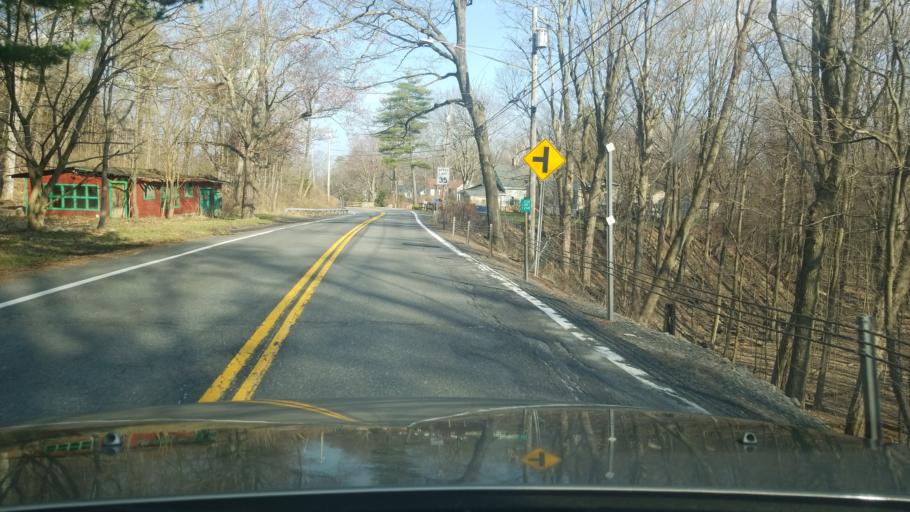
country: US
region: New York
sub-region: Greene County
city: Palenville
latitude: 42.1756
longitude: -74.0286
